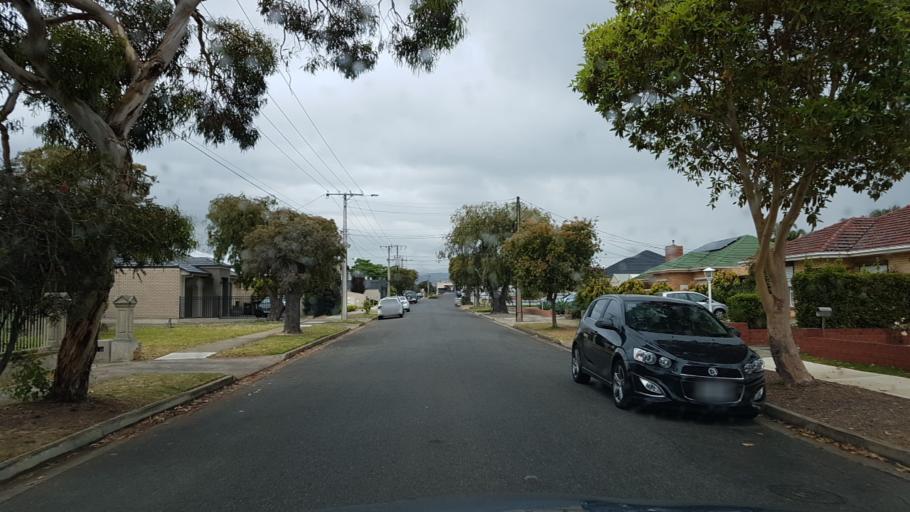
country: AU
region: South Australia
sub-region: Marion
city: South Plympton
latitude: -34.9765
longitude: 138.5538
